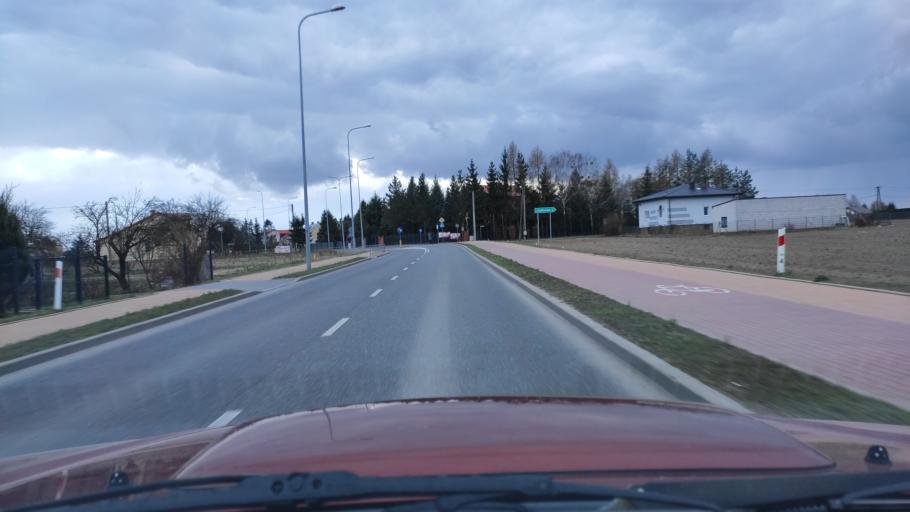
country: PL
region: Masovian Voivodeship
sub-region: Powiat zwolenski
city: Zwolen
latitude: 51.3730
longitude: 21.5882
